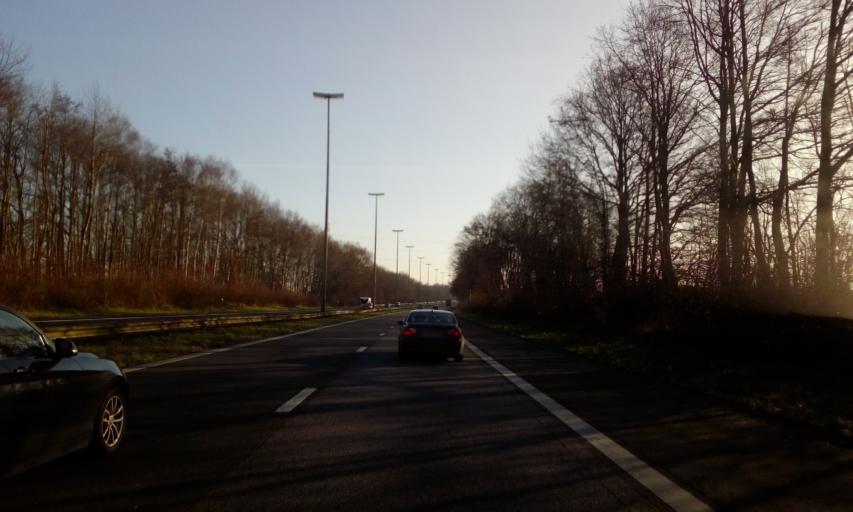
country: BE
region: Wallonia
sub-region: Province du Hainaut
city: Pont-a-Celles
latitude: 50.5545
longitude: 4.3632
